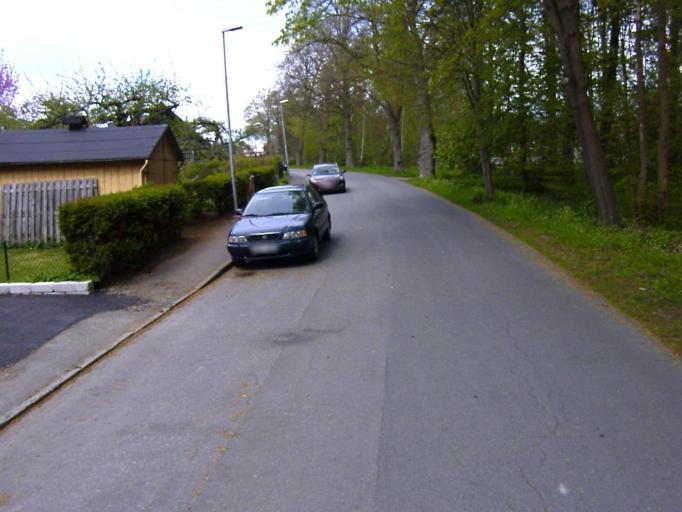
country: SE
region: Skane
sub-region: Kristianstads Kommun
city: Kristianstad
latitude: 56.0359
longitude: 14.1743
